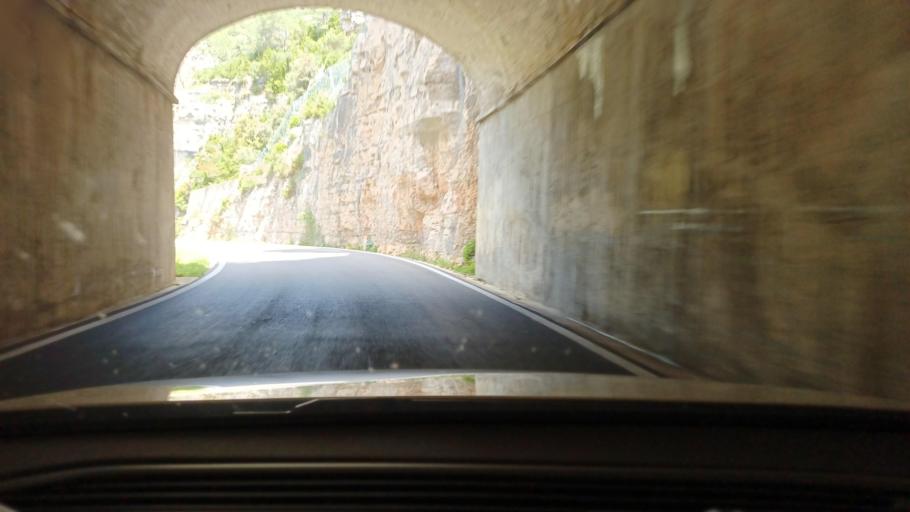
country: ES
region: Valencia
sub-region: Provincia de Castello
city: Rosell
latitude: 40.6700
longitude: 0.2374
